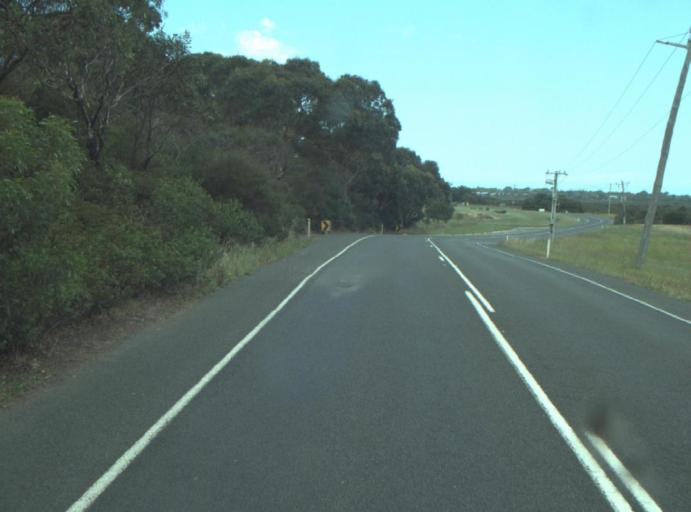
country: AU
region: Victoria
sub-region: Greater Geelong
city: Leopold
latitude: -38.2490
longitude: 144.5044
